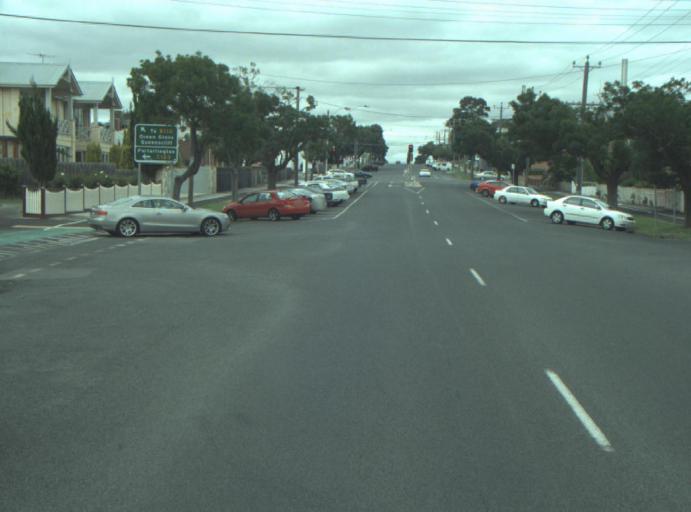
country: AU
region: Victoria
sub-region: Greater Geelong
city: East Geelong
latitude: -38.1501
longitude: 144.3680
